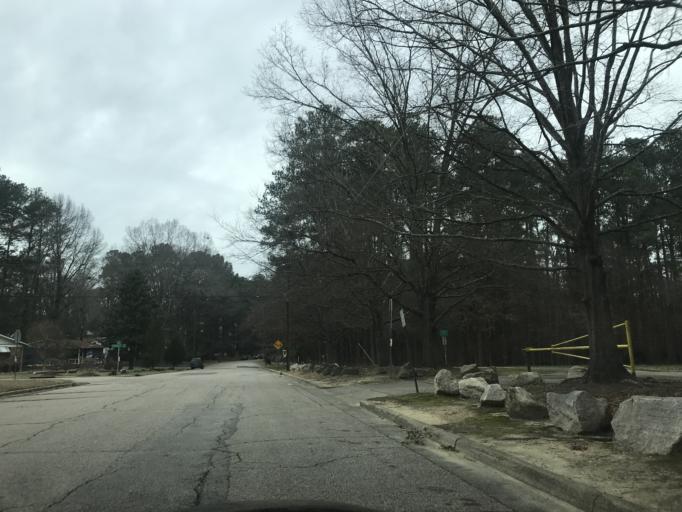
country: US
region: North Carolina
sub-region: Wake County
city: Raleigh
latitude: 35.7943
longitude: -78.5981
